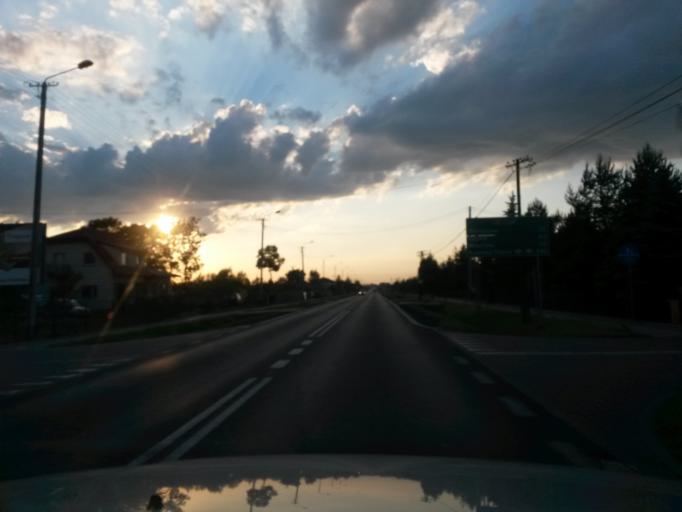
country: PL
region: Lodz Voivodeship
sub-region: Powiat wielunski
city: Wielun
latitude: 51.2336
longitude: 18.5383
